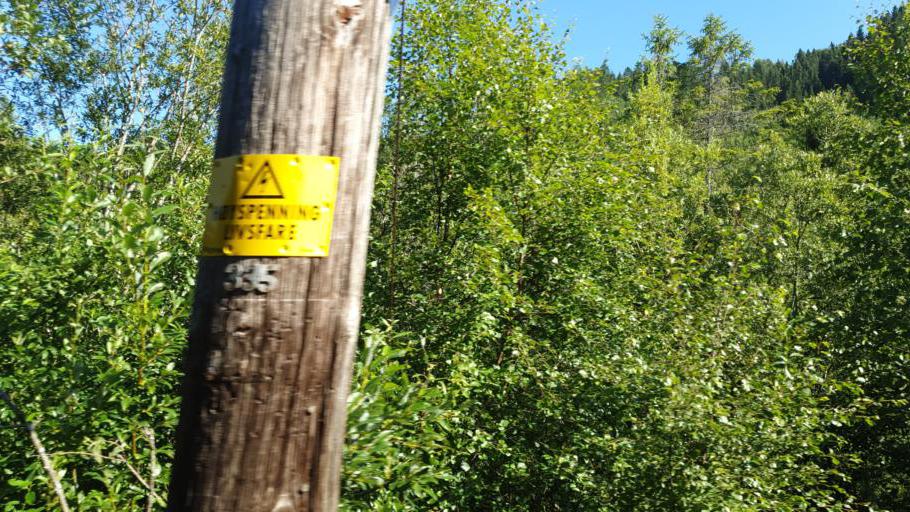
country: NO
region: Sor-Trondelag
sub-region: Orkdal
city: Orkanger
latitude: 63.1951
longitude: 9.7864
